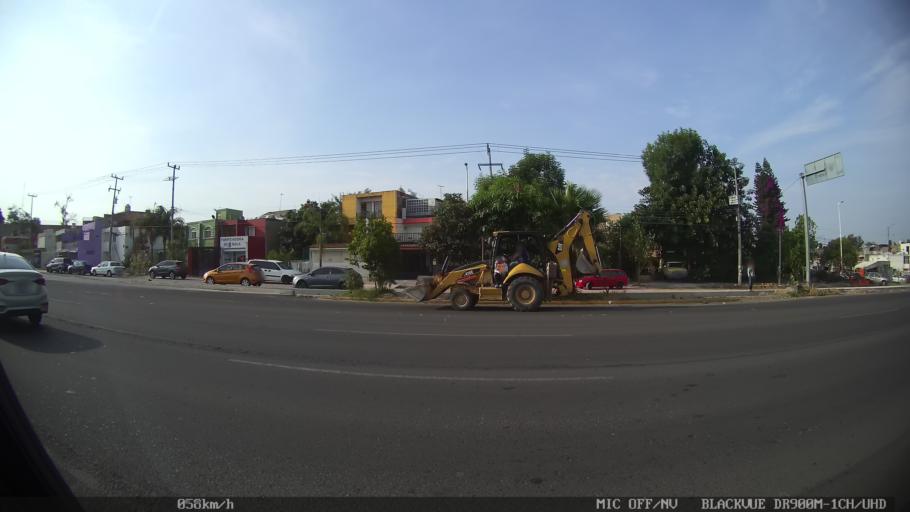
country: MX
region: Jalisco
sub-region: Zapopan
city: Zapopan
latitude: 20.7198
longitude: -103.3223
